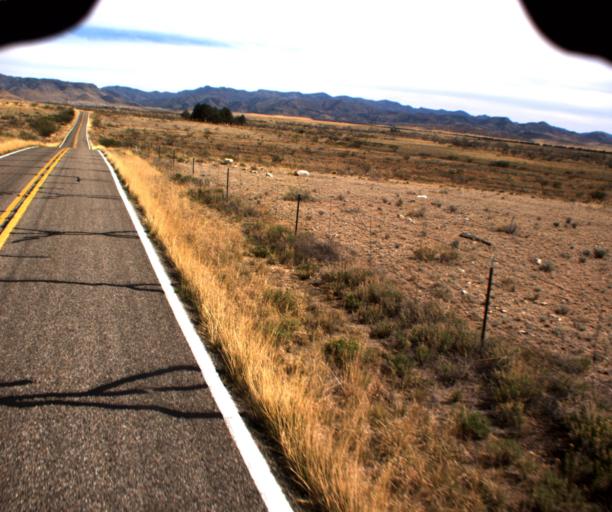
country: US
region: Arizona
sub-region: Cochise County
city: Willcox
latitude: 32.0310
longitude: -109.4673
